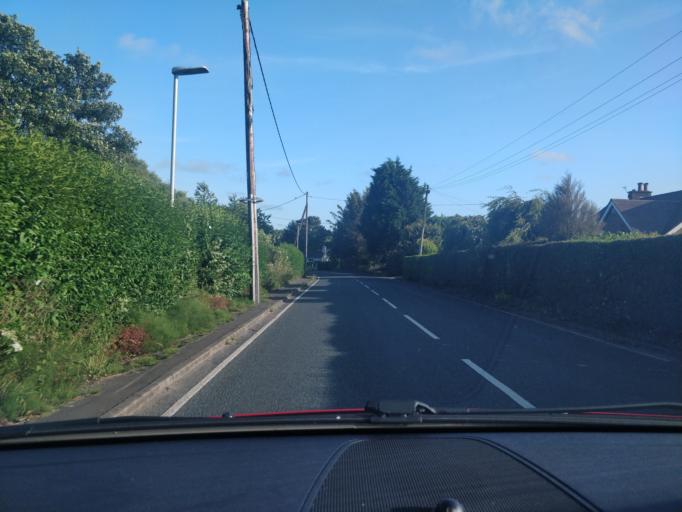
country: GB
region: England
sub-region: Lancashire
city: Tarleton
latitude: 53.6423
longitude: -2.8507
